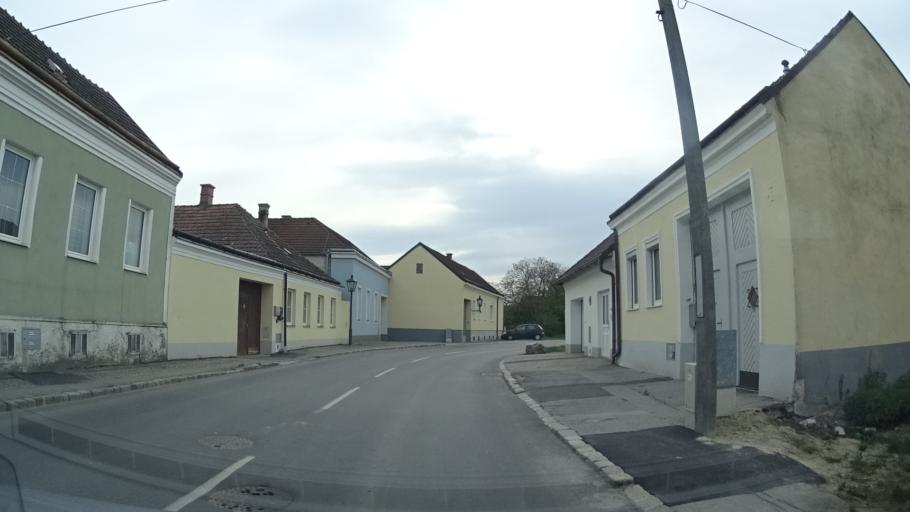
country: AT
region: Lower Austria
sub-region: Politischer Bezirk Korneuburg
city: Leobendorf
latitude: 48.3771
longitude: 16.3279
